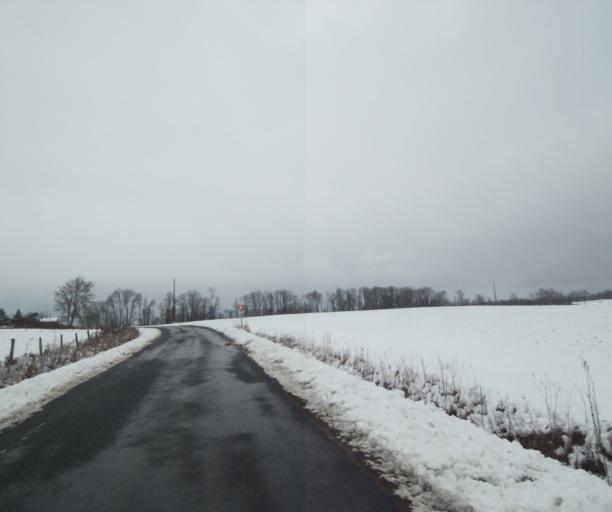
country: FR
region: Champagne-Ardenne
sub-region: Departement de la Haute-Marne
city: Laneuville-a-Remy
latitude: 48.4912
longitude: 4.8675
